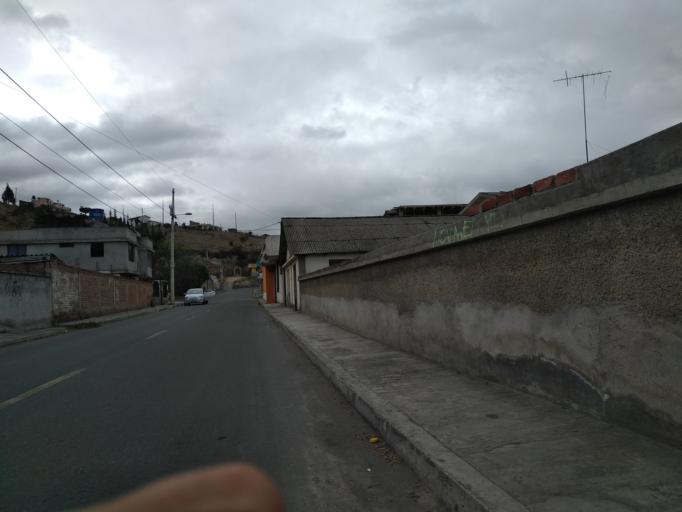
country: EC
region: Chimborazo
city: Riobamba
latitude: -1.6869
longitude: -78.6785
